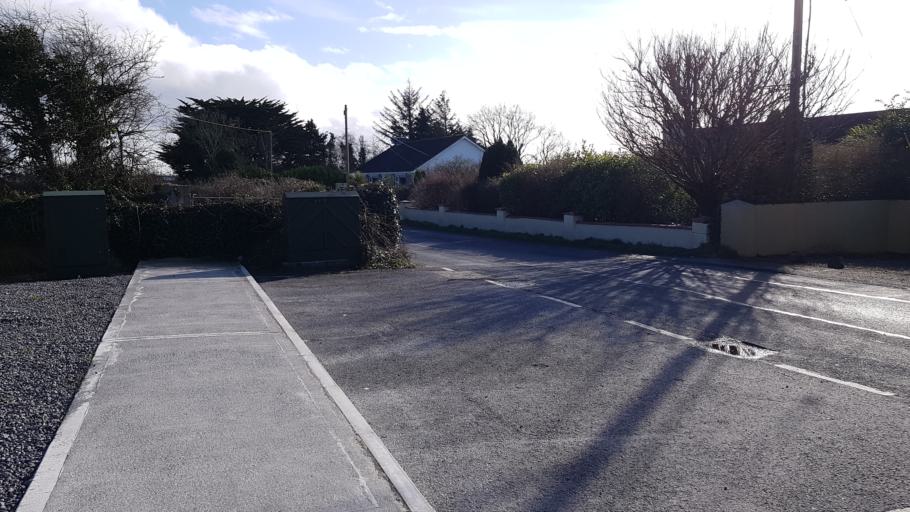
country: IE
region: Connaught
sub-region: County Galway
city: Gaillimh
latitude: 53.3015
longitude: -9.0193
